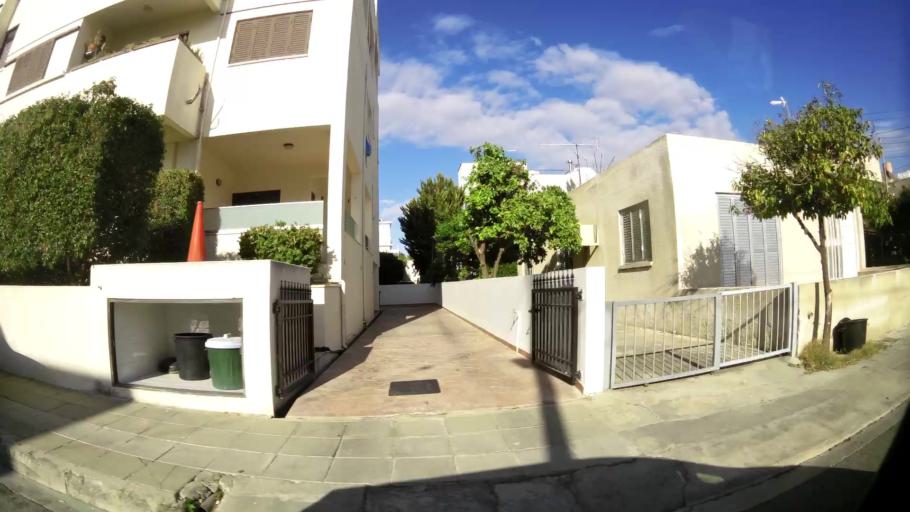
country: CY
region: Lefkosia
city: Nicosia
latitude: 35.1372
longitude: 33.3630
